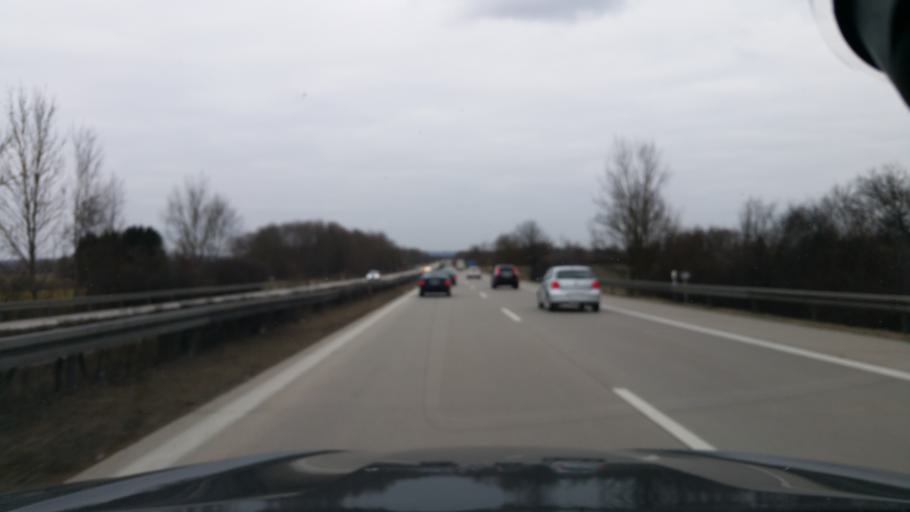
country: DE
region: Bavaria
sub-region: Upper Bavaria
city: Langenpreising
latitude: 48.4672
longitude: 11.9806
